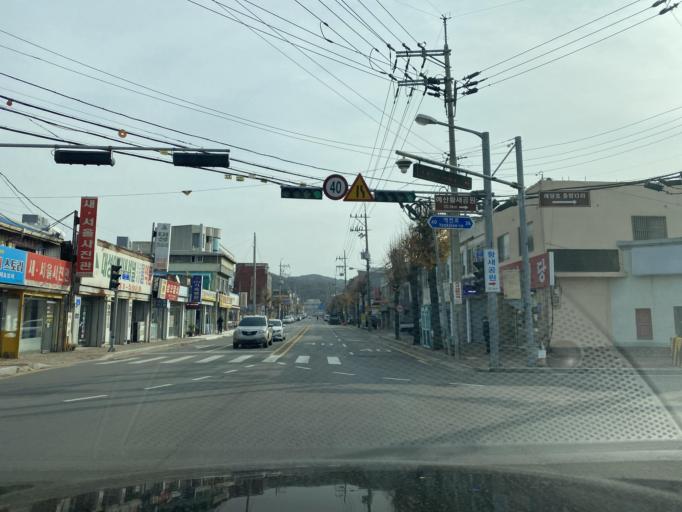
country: KR
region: Chungcheongnam-do
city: Yesan
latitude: 36.6824
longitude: 126.8290
